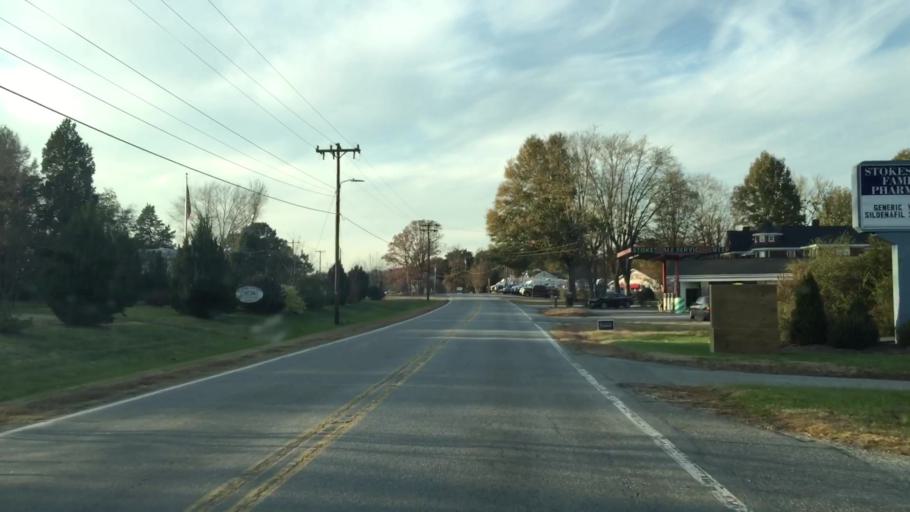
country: US
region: North Carolina
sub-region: Guilford County
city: Stokesdale
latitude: 36.2424
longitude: -79.9852
